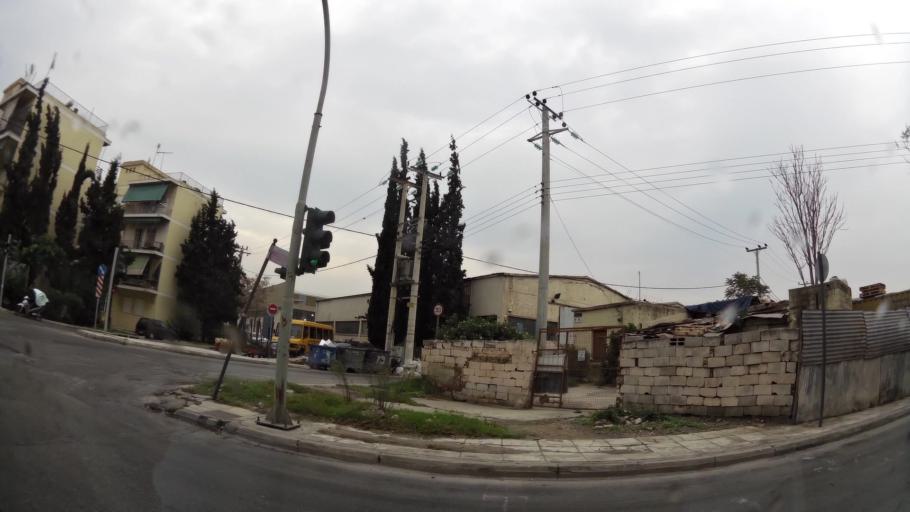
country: GR
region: Attica
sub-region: Nomos Piraios
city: Agios Ioannis Rentis
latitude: 37.9661
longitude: 23.6672
